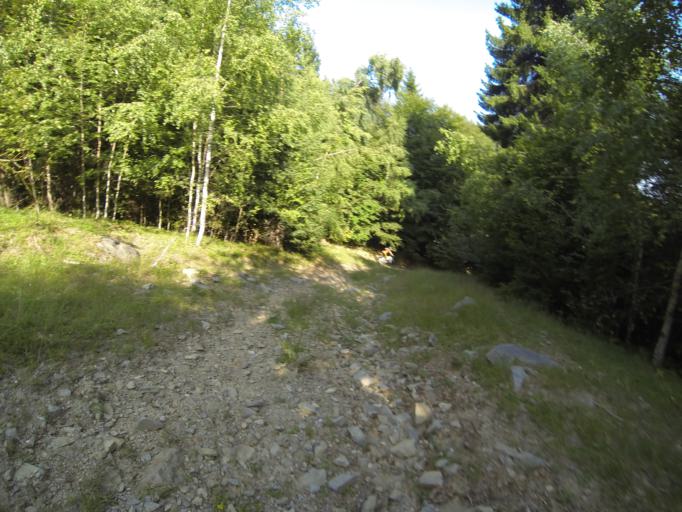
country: RO
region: Valcea
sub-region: Comuna Vaideeni
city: Vaideeni
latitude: 45.2337
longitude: 23.9625
